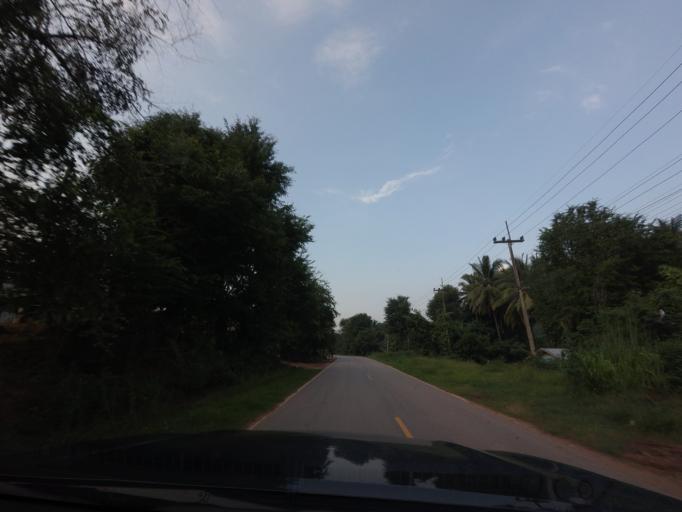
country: TH
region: Loei
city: Na Haeo
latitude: 17.4381
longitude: 101.0536
